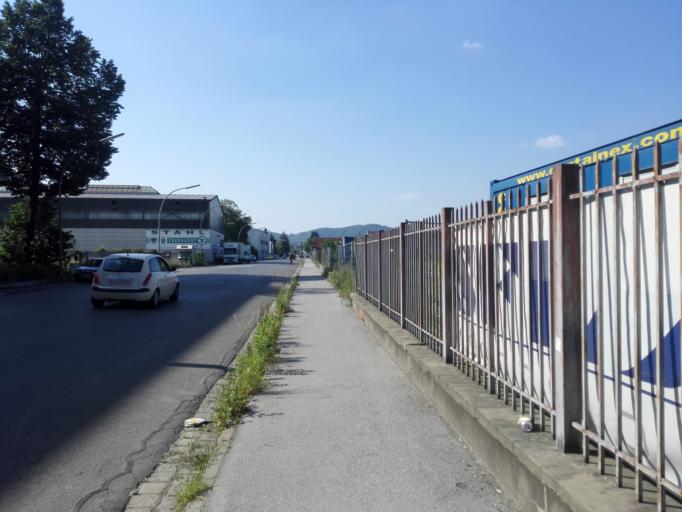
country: AT
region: Styria
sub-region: Graz Stadt
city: Goesting
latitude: 47.0803
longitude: 15.4106
